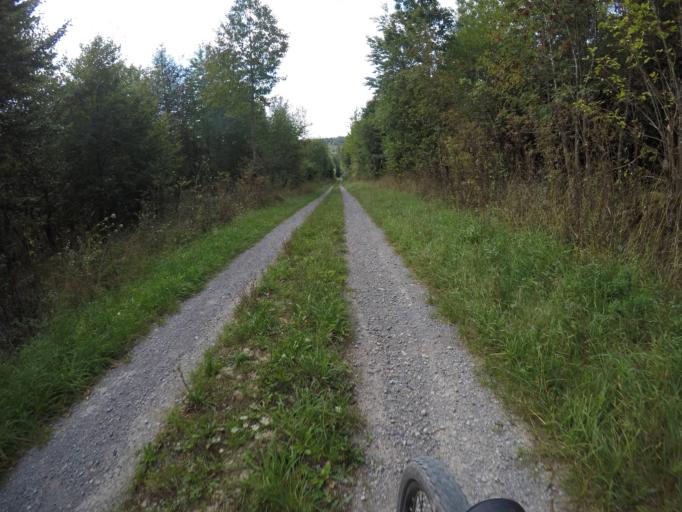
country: DE
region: Baden-Wuerttemberg
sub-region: Regierungsbezirk Stuttgart
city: Deckenpfronn
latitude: 48.6735
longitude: 8.8208
